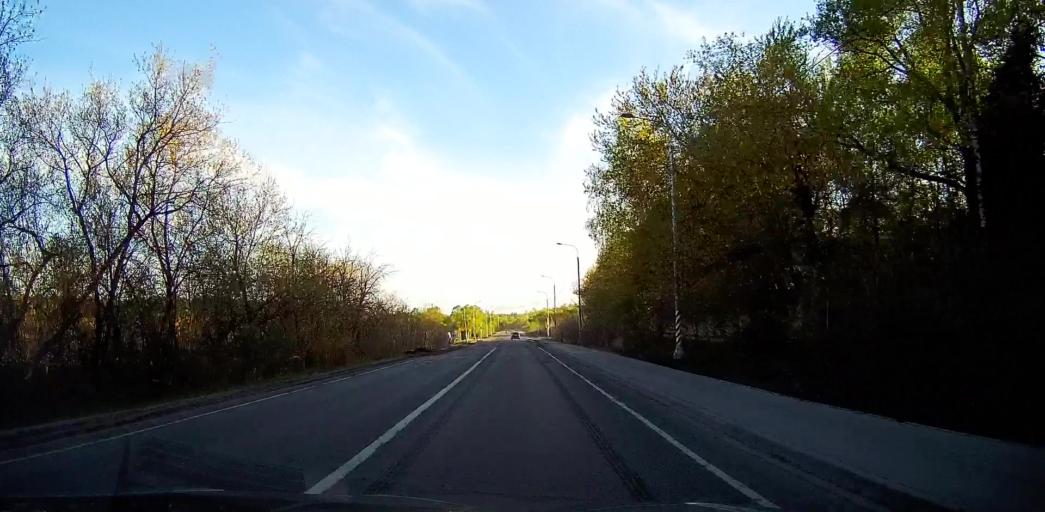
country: RU
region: Moskovskaya
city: Bronnitsy
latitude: 55.3095
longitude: 38.2138
